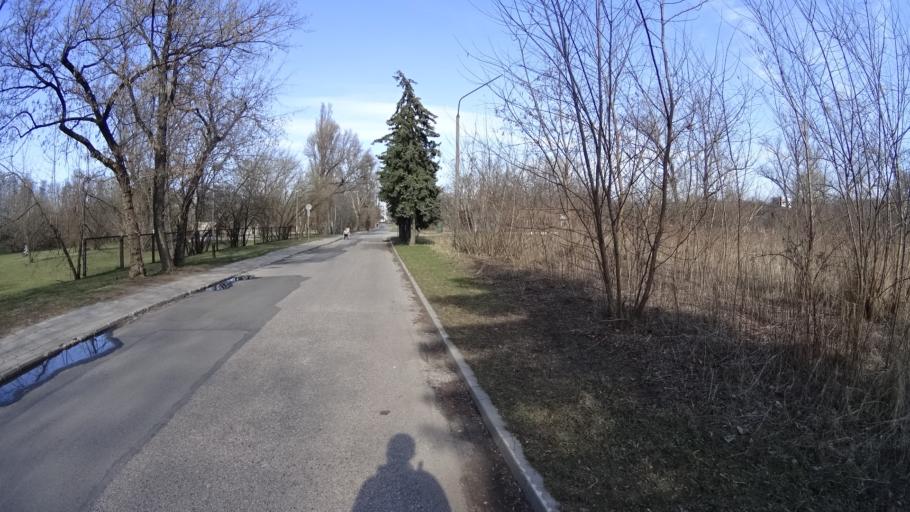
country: PL
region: Masovian Voivodeship
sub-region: Warszawa
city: Bielany
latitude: 52.2599
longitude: 20.9470
